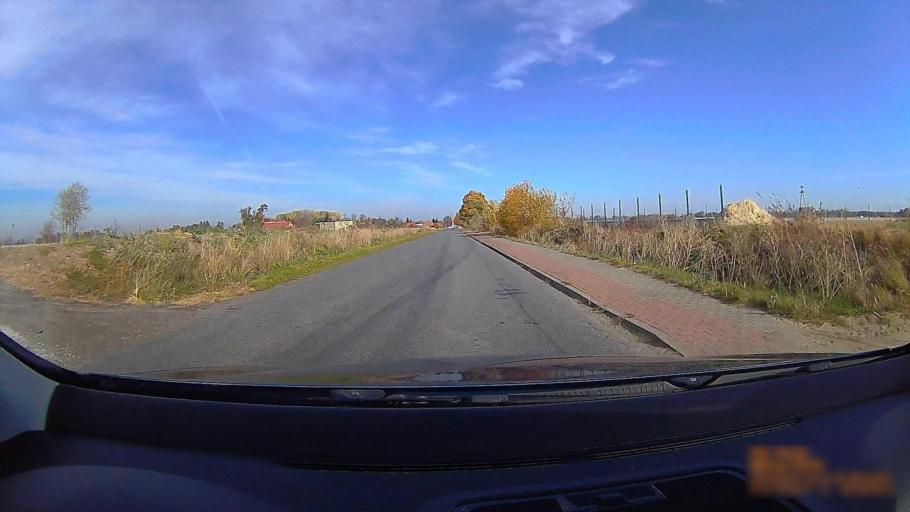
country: PL
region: Greater Poland Voivodeship
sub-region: Powiat ostrzeszowski
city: Doruchow
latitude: 51.4073
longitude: 18.0715
